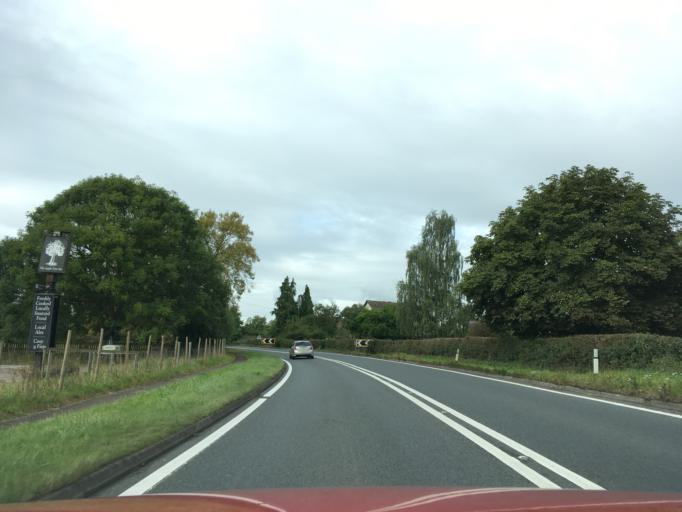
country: GB
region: England
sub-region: Gloucestershire
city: Gloucester
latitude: 51.8565
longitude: -2.3093
